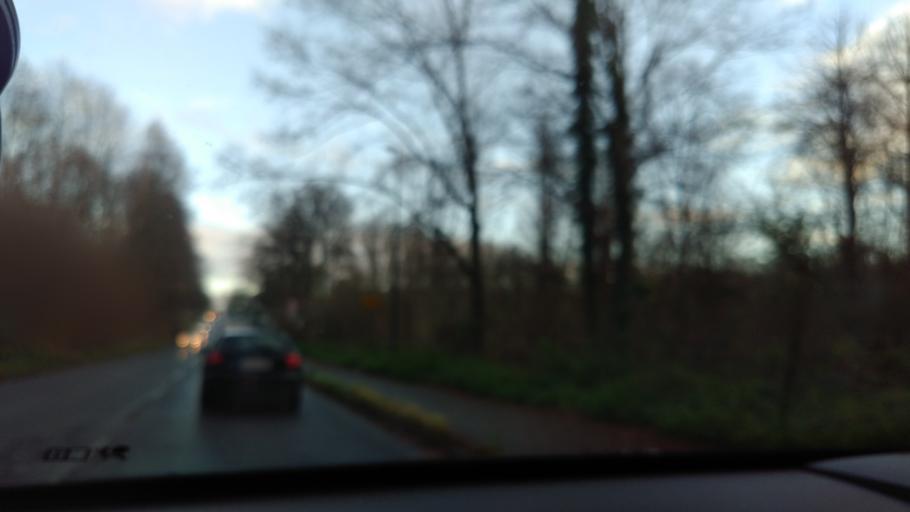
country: DE
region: North Rhine-Westphalia
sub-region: Regierungsbezirk Dusseldorf
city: Essen
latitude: 51.4146
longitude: 6.9543
